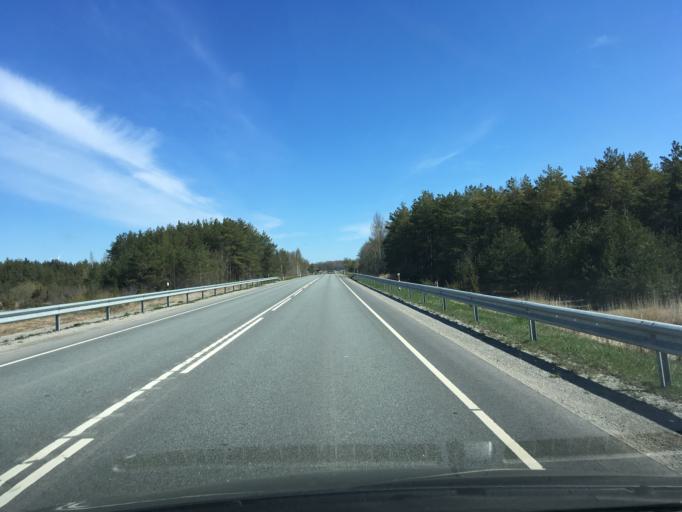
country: EE
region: Laeaene
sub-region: Lihula vald
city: Lihula
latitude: 58.5918
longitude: 23.5406
